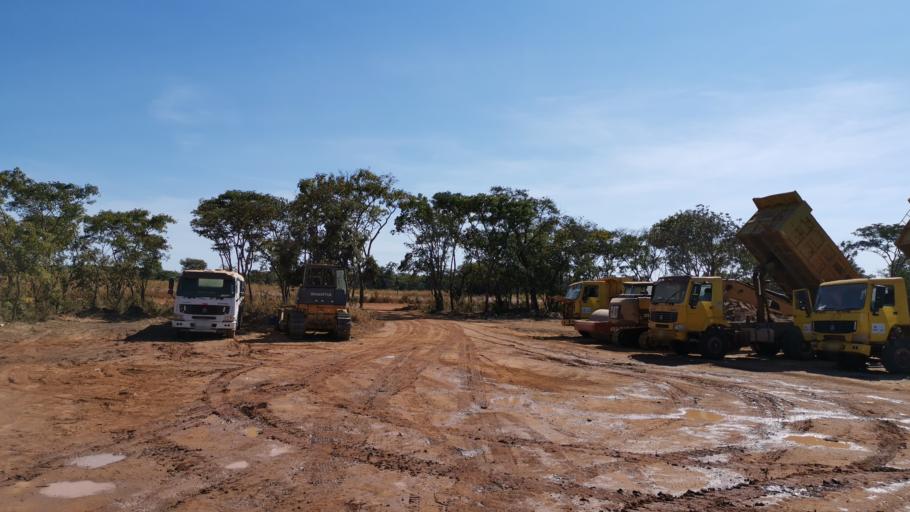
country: ZM
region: Central
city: Mkushi
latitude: -13.9924
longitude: 29.5290
